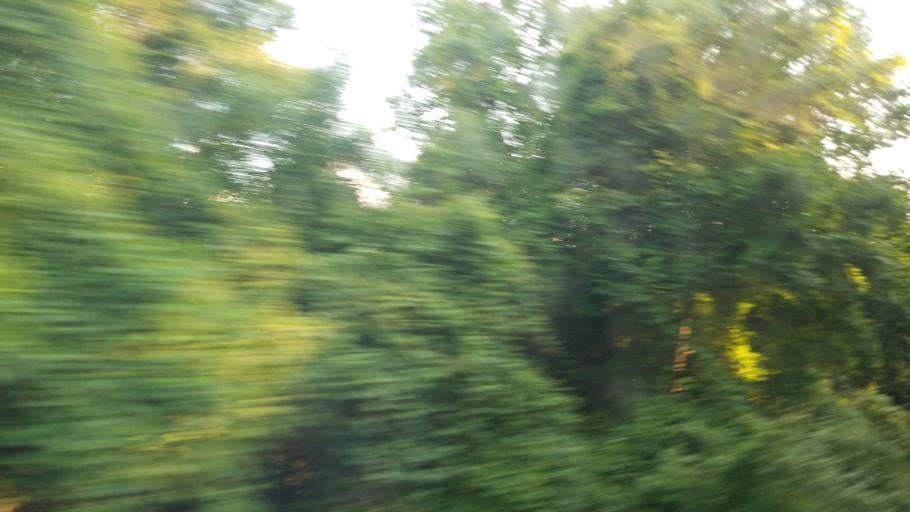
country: US
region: Virginia
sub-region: Fairfax County
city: North Springfield
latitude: 38.7950
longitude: -77.1992
